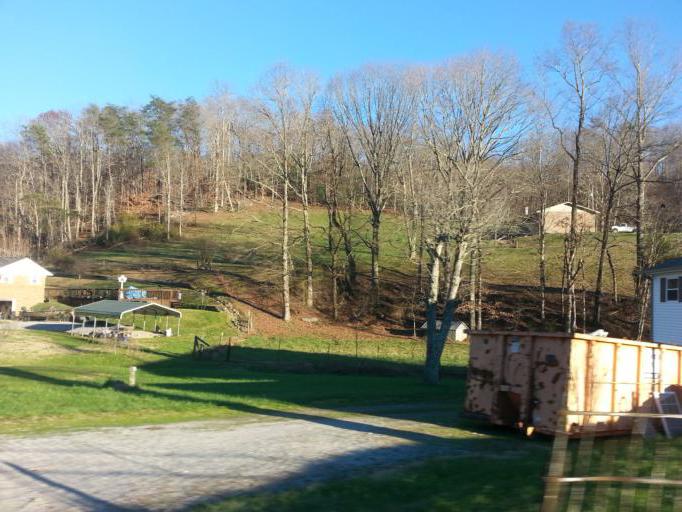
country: US
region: Tennessee
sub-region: Anderson County
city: Rocky Top
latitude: 36.1834
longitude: -84.1603
